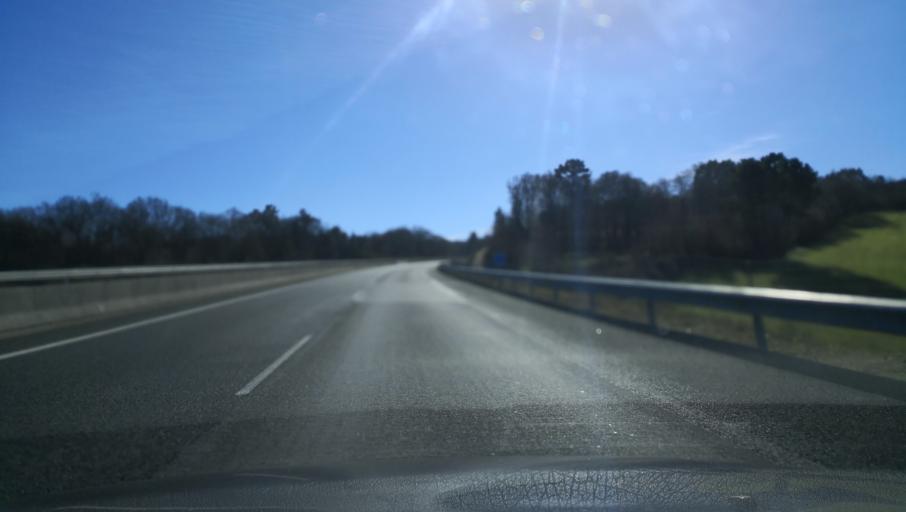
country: ES
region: Galicia
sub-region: Provincia de Pontevedra
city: Lalin
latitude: 42.6608
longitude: -8.1437
